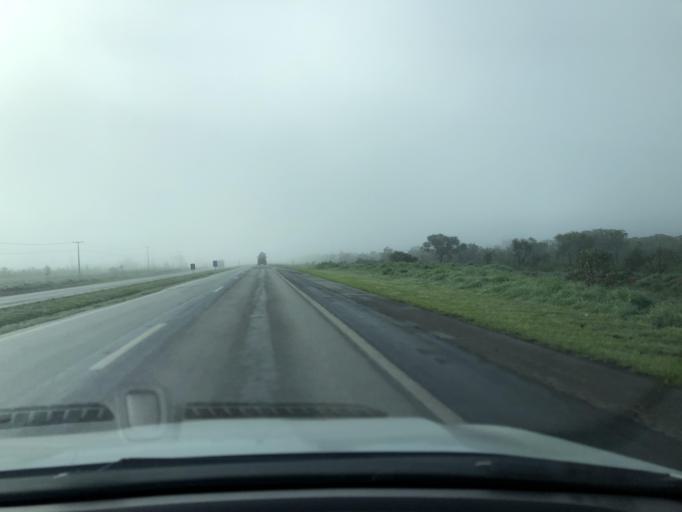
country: BR
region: Goias
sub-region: Luziania
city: Luziania
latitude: -16.2835
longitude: -47.8577
